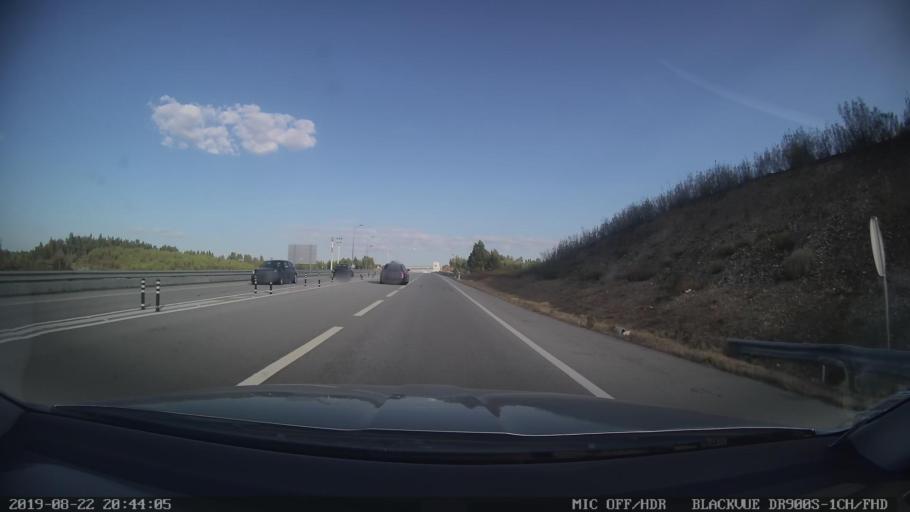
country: PT
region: Castelo Branco
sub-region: Proenca-A-Nova
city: Proenca-a-Nova
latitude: 39.7043
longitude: -7.8449
